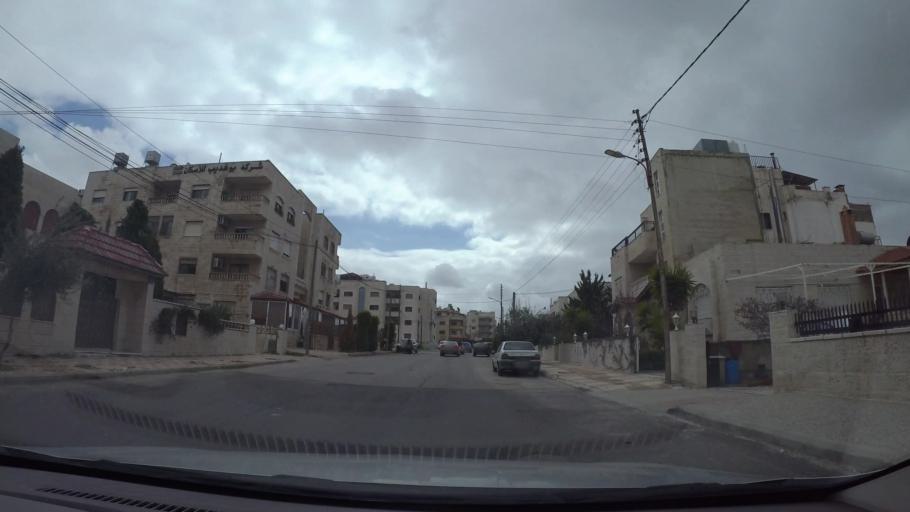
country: JO
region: Amman
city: Al Jubayhah
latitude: 31.9926
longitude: 35.8453
